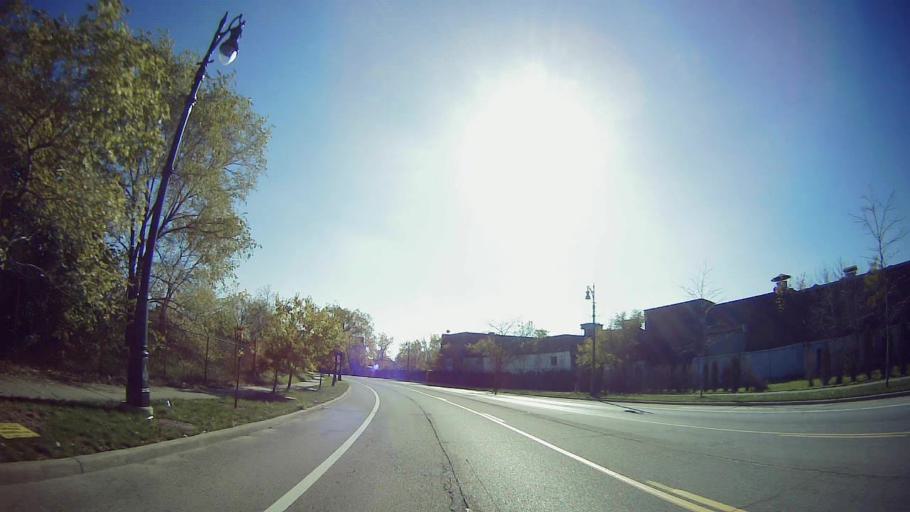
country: US
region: Michigan
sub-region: Wayne County
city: Highland Park
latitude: 42.3613
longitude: -83.0837
